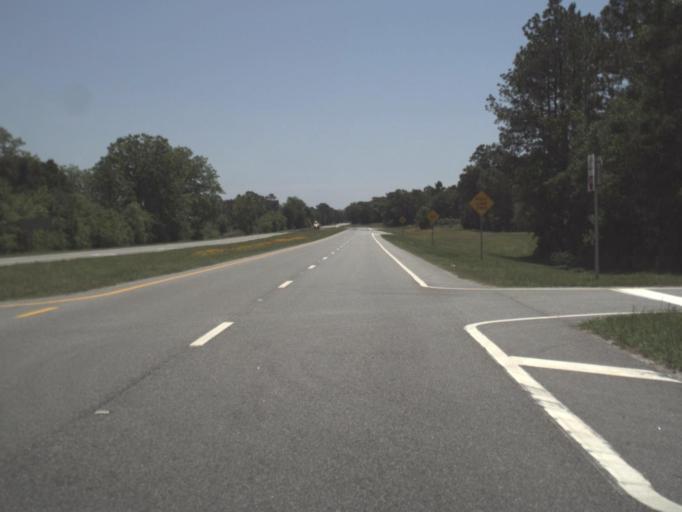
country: US
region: Florida
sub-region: Suwannee County
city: Live Oak
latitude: 30.3429
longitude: -83.0894
